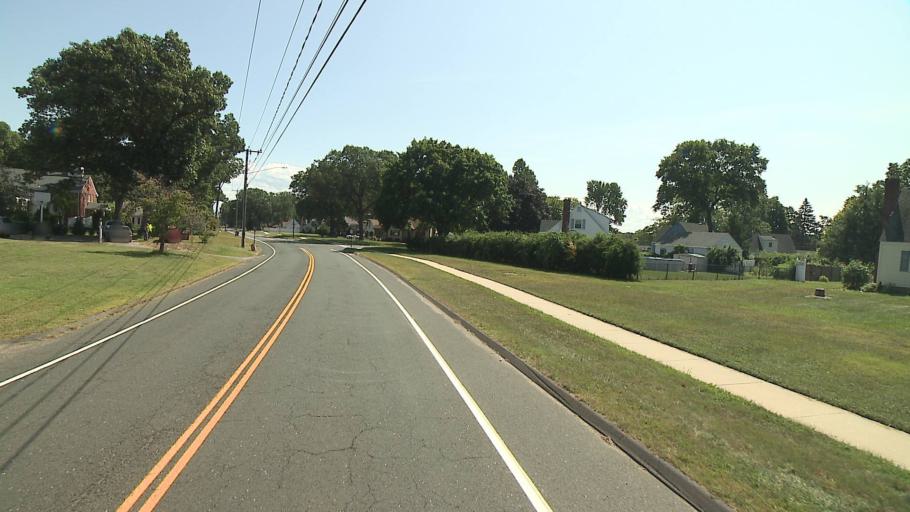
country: US
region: Connecticut
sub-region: Hartford County
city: Windsor Locks
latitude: 41.9268
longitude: -72.6617
